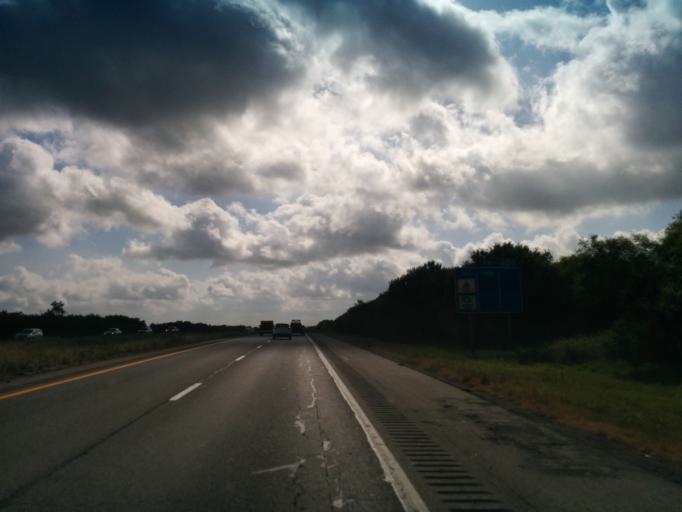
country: US
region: Texas
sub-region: Caldwell County
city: Luling
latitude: 29.6503
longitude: -97.6772
